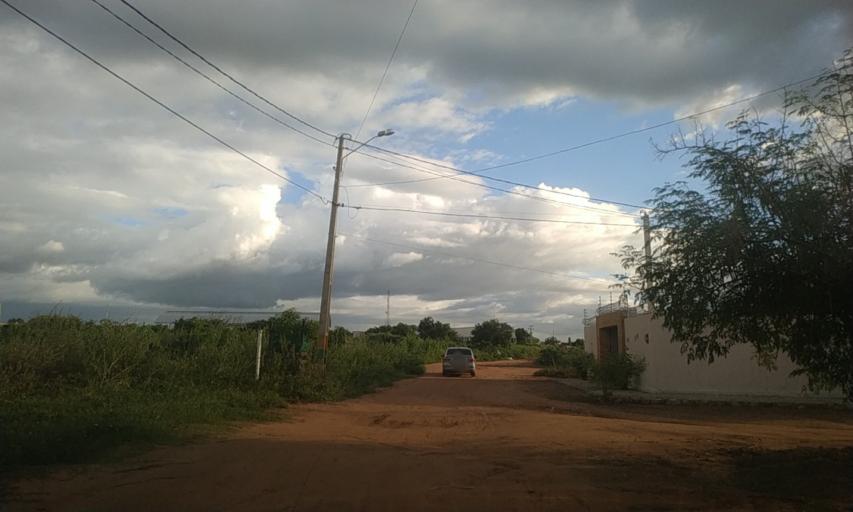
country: BR
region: Rio Grande do Norte
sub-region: Mossoro
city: Mossoro
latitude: -5.2228
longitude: -37.3408
